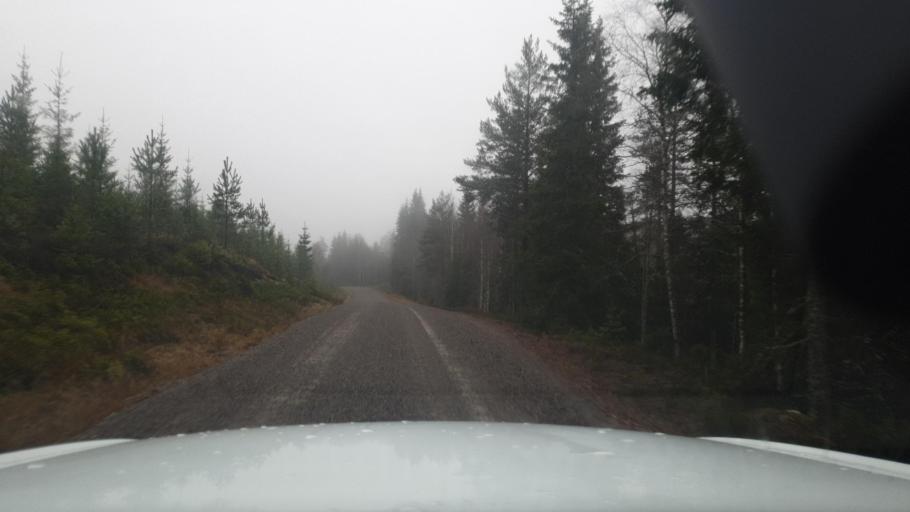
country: SE
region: Vaermland
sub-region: Eda Kommun
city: Charlottenberg
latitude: 60.1145
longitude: 12.6034
